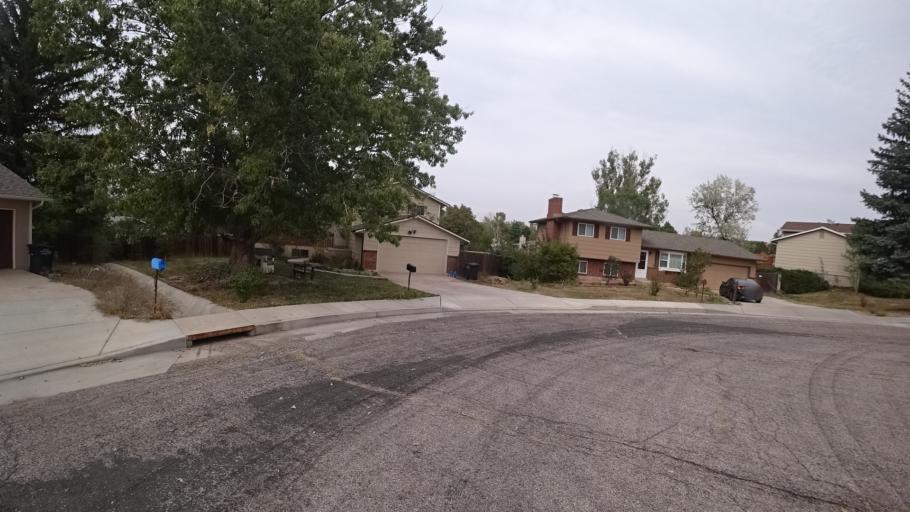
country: US
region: Colorado
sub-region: El Paso County
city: Cimarron Hills
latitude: 38.8992
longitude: -104.7359
